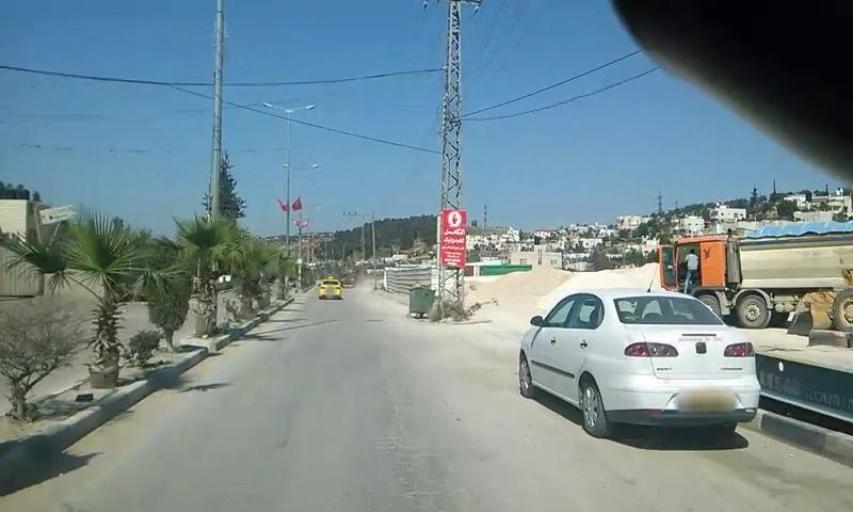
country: PS
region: West Bank
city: Idhna
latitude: 31.5697
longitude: 34.9809
